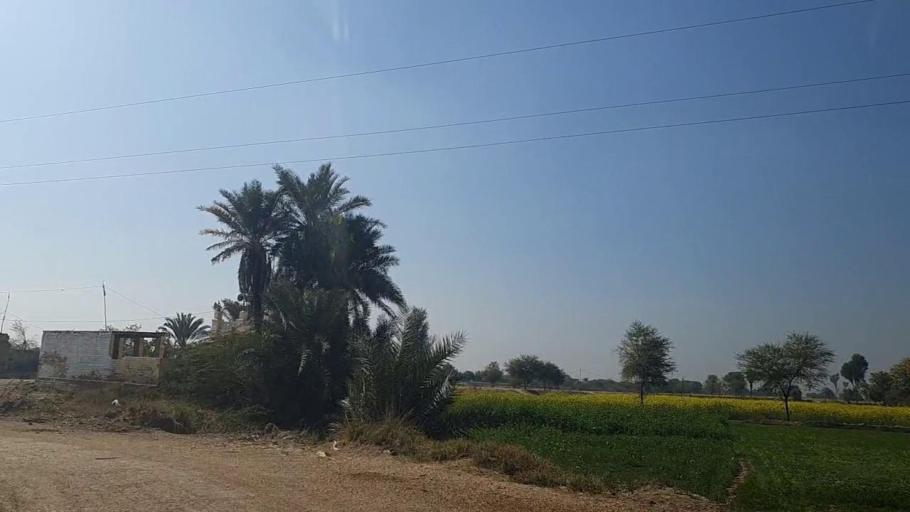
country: PK
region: Sindh
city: Nawabshah
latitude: 26.2301
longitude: 68.3413
